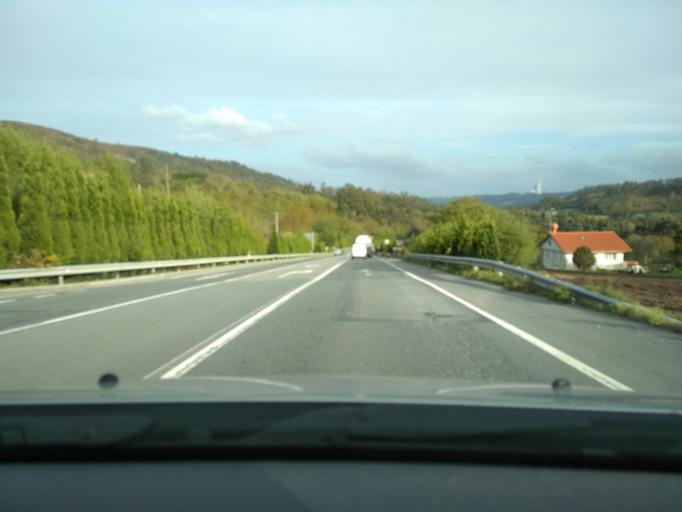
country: ES
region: Galicia
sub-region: Provincia da Coruna
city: Cerceda
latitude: 43.2261
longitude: -8.4629
